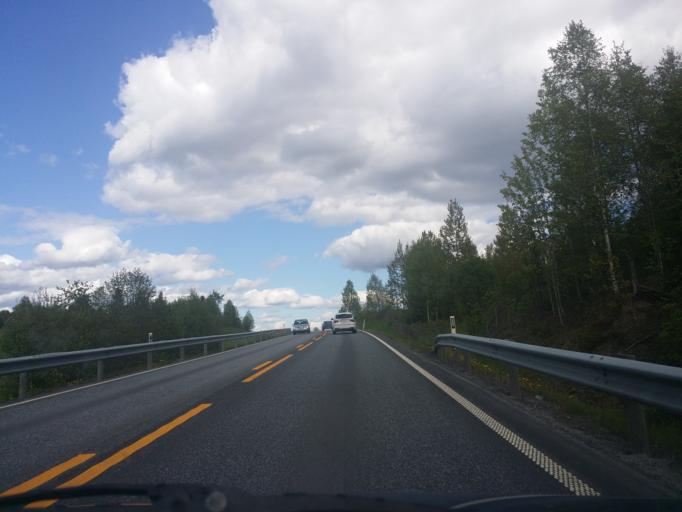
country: NO
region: Oppland
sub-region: Lunner
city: Roa
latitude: 60.2901
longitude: 10.5550
